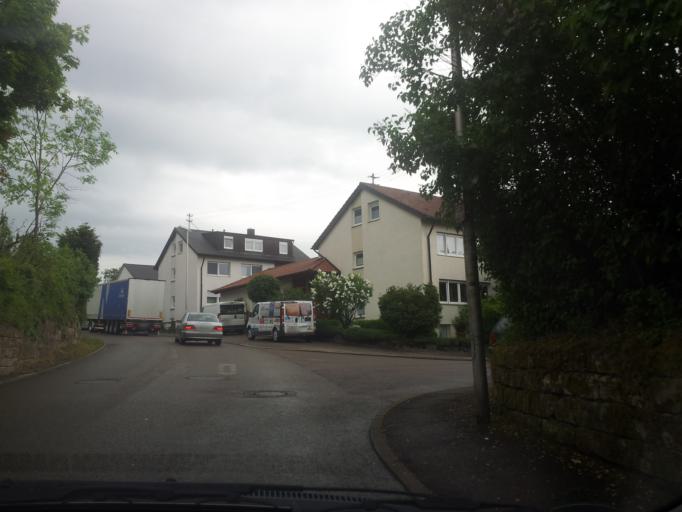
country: DE
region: Baden-Wuerttemberg
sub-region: Regierungsbezirk Stuttgart
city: Beilstein
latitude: 49.0399
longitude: 9.3193
